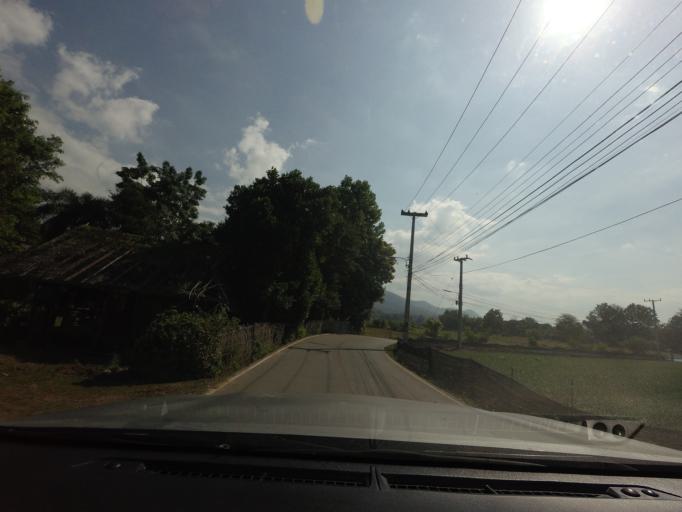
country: TH
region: Mae Hong Son
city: Wiang Nuea
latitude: 19.3875
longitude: 98.4409
